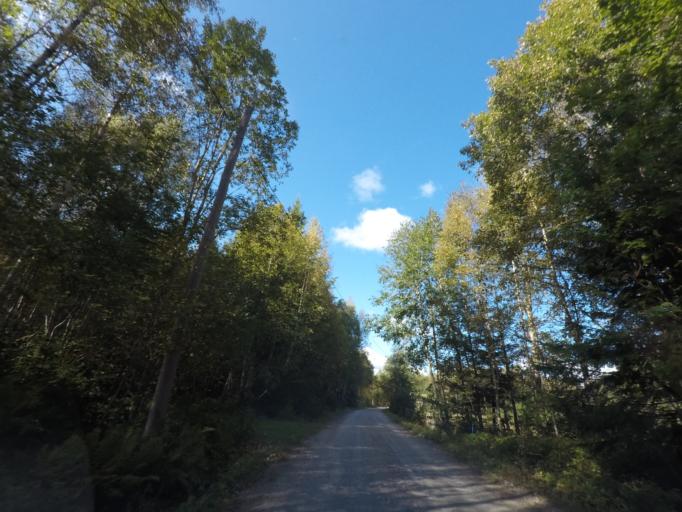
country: SE
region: Vaestmanland
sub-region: Skinnskattebergs Kommun
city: Skinnskatteberg
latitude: 59.8301
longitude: 15.5285
